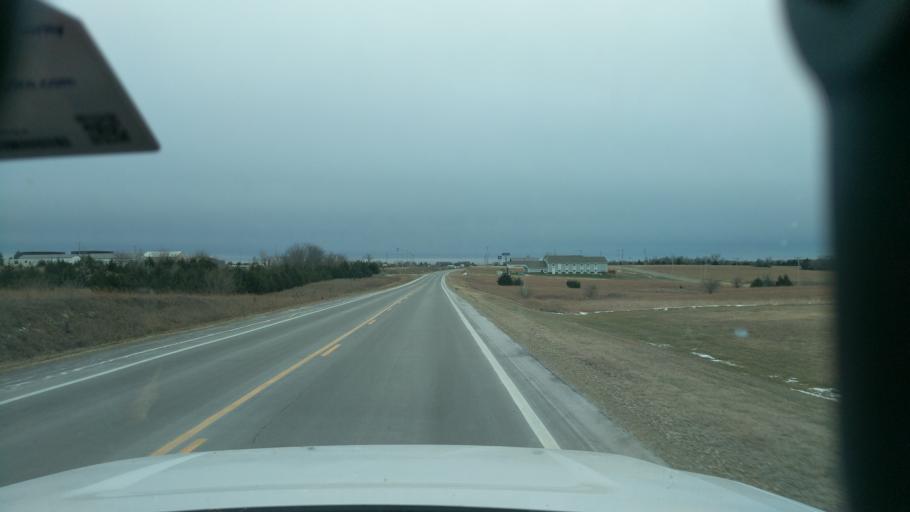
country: US
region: Kansas
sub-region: Dickinson County
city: Herington
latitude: 38.6812
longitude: -96.9305
